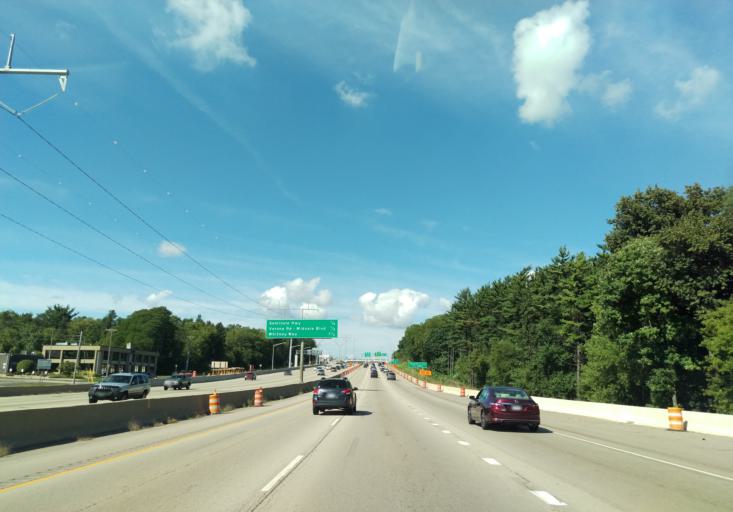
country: US
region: Wisconsin
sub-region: Dane County
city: Shorewood Hills
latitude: 43.0352
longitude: -89.4338
